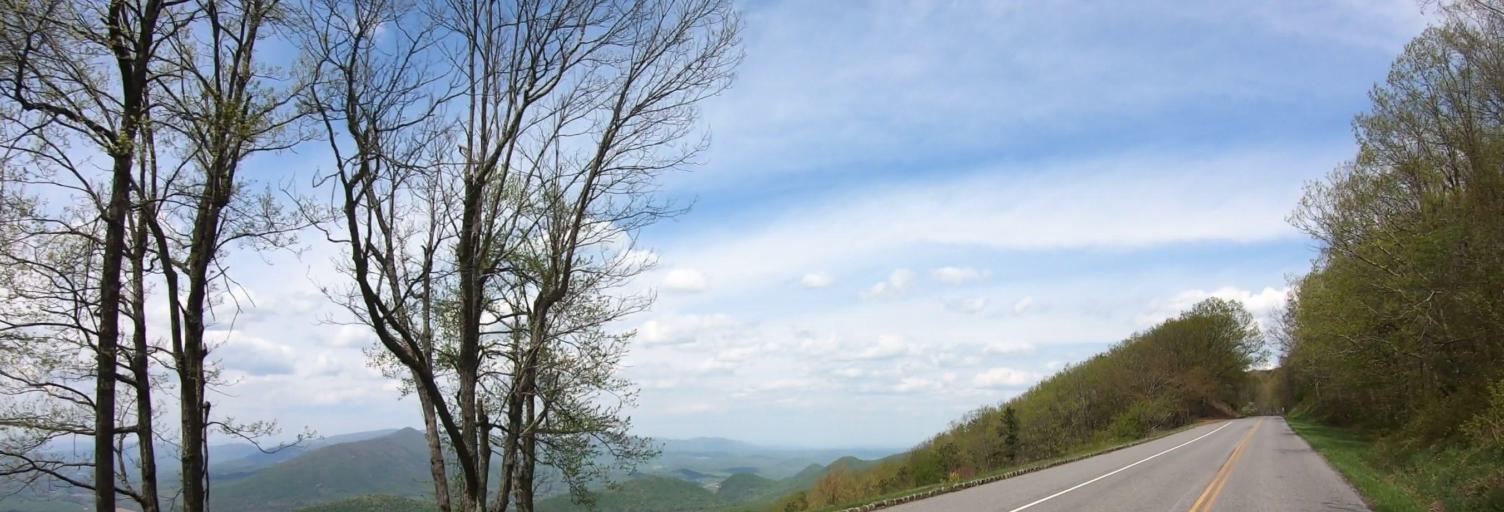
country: US
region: Virginia
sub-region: Botetourt County
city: Buchanan
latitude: 37.4779
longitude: -79.6876
